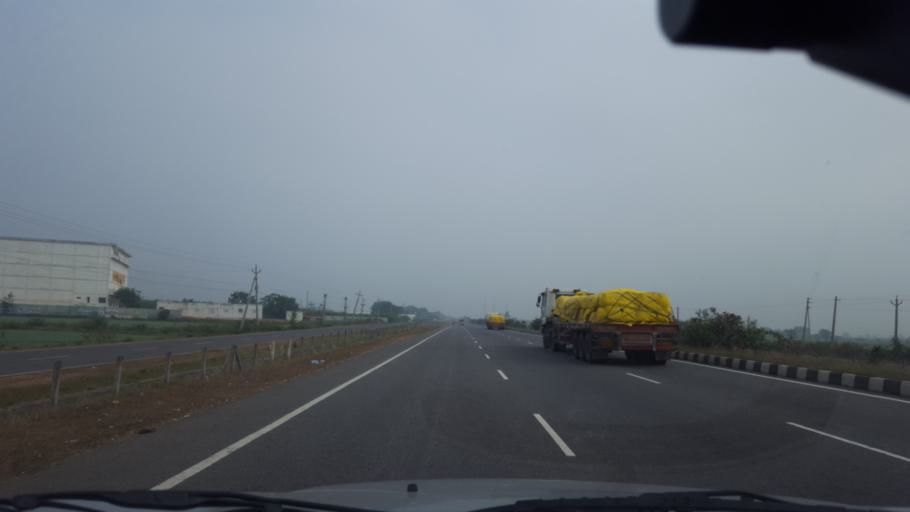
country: IN
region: Andhra Pradesh
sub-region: Guntur
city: Chilakalurupet
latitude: 16.0379
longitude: 80.1339
